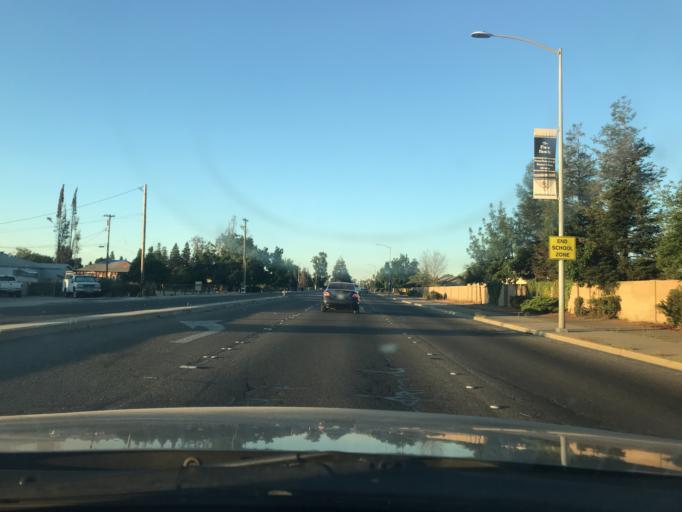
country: US
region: California
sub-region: Merced County
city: Atwater
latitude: 37.3466
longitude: -120.5769
